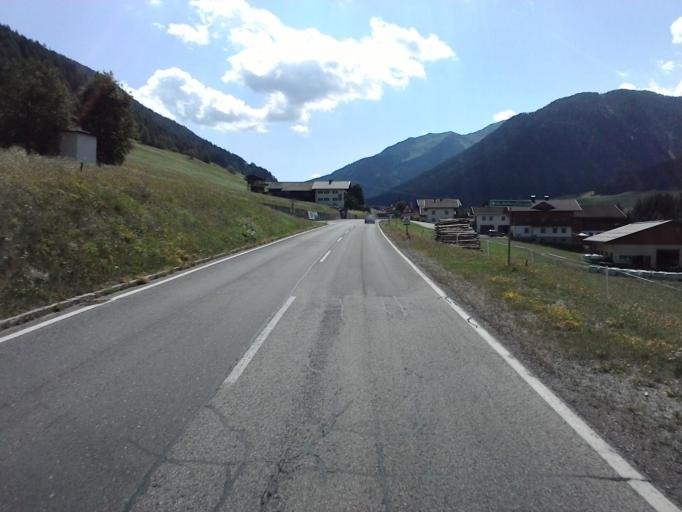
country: AT
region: Tyrol
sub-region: Politischer Bezirk Lienz
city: Kartitsch
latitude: 46.7327
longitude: 12.4847
